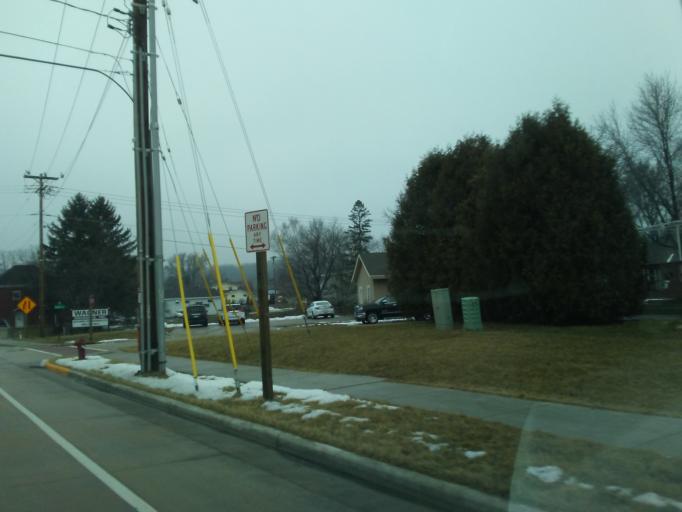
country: US
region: Wisconsin
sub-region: Dane County
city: Cross Plains
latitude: 43.1116
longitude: -89.6454
